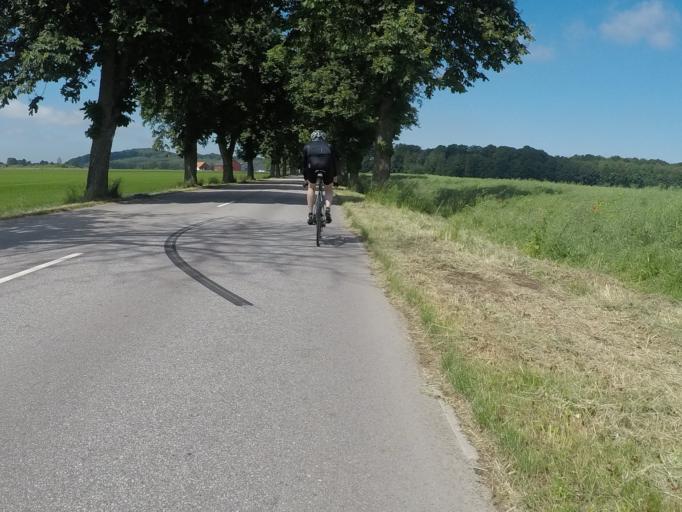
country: SE
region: Skane
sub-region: Malmo
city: Oxie
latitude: 55.5272
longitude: 13.1574
